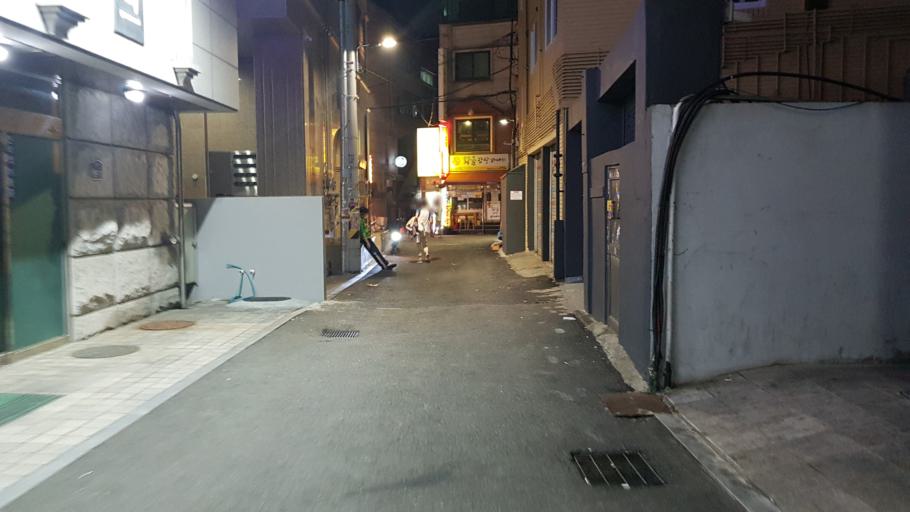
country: KR
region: Gyeonggi-do
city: Kwangmyong
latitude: 37.4845
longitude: 126.9275
